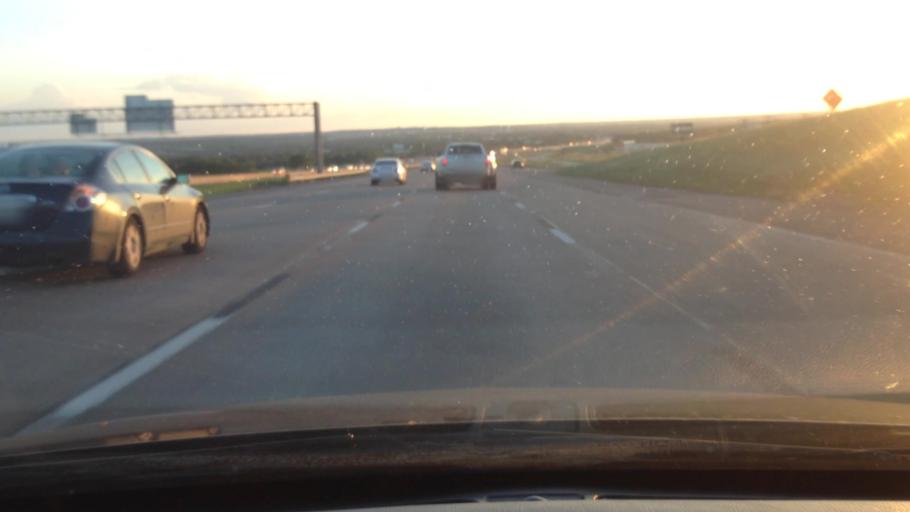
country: US
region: Texas
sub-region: Tarrant County
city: Lake Worth
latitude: 32.8023
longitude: -97.4301
